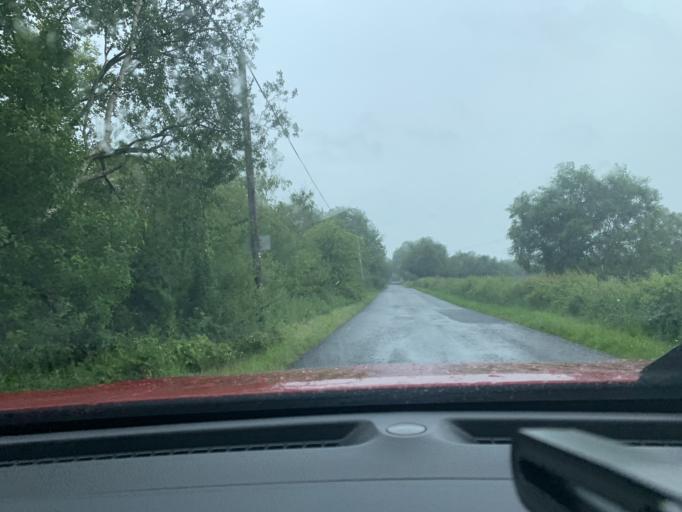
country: GB
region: Northern Ireland
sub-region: Fermanagh District
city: Enniskillen
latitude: 54.2875
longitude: -7.7197
